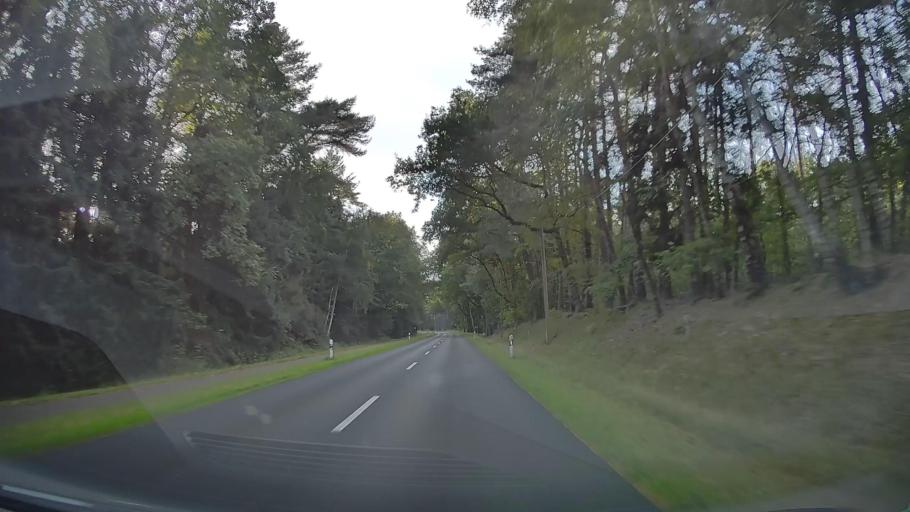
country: DE
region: Lower Saxony
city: Hellwege
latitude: 53.0734
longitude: 9.2087
